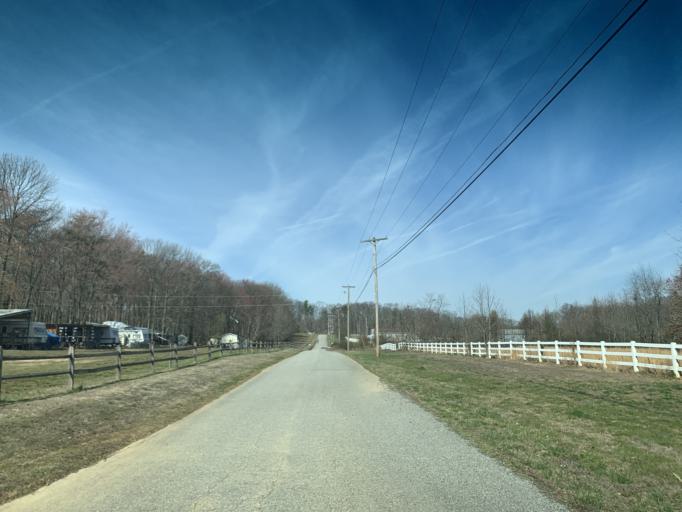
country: US
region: Maryland
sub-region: Cecil County
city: Charlestown
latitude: 39.5536
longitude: -76.0078
